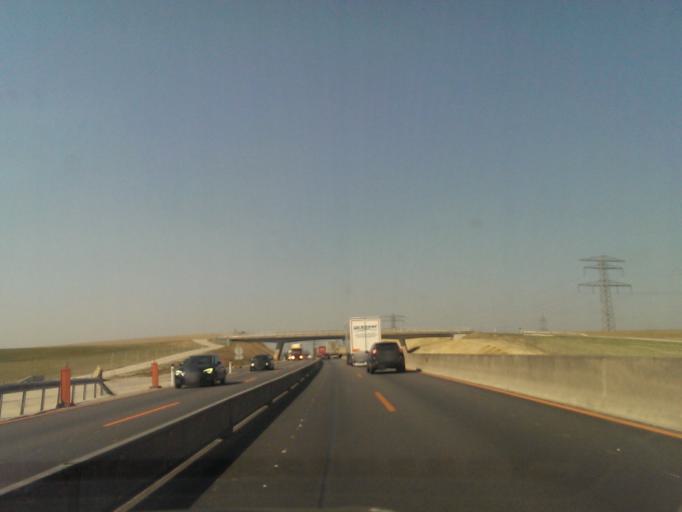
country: AT
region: Upper Austria
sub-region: Politischer Bezirk Vocklabruck
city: Wolfsegg am Hausruck
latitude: 48.1846
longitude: 13.6882
